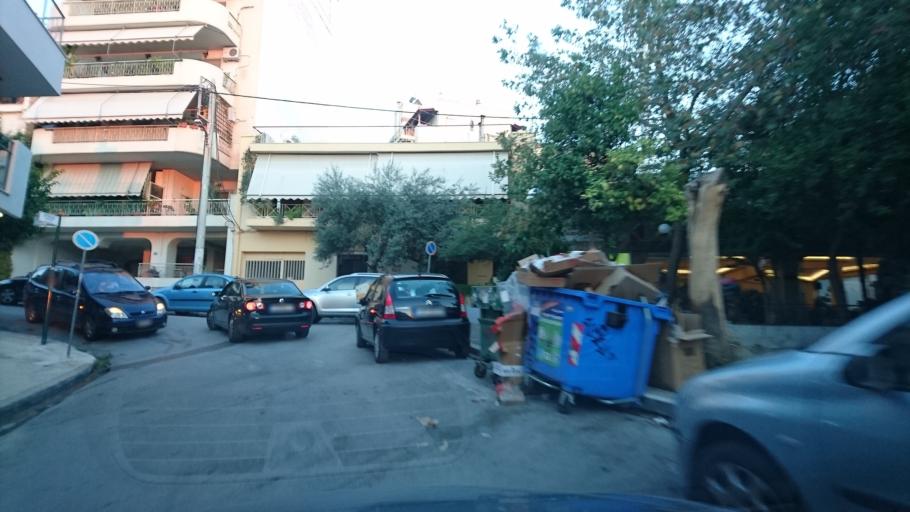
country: GR
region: Attica
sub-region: Nomarchia Athinas
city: Ilioupoli
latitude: 37.9370
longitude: 23.7646
